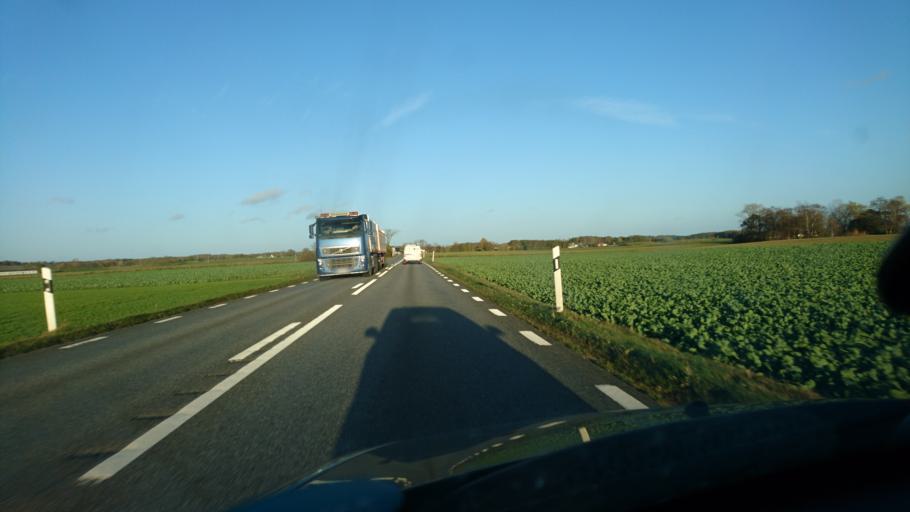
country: SE
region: Skane
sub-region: Tomelilla Kommun
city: Tomelilla
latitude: 55.5488
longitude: 14.0619
